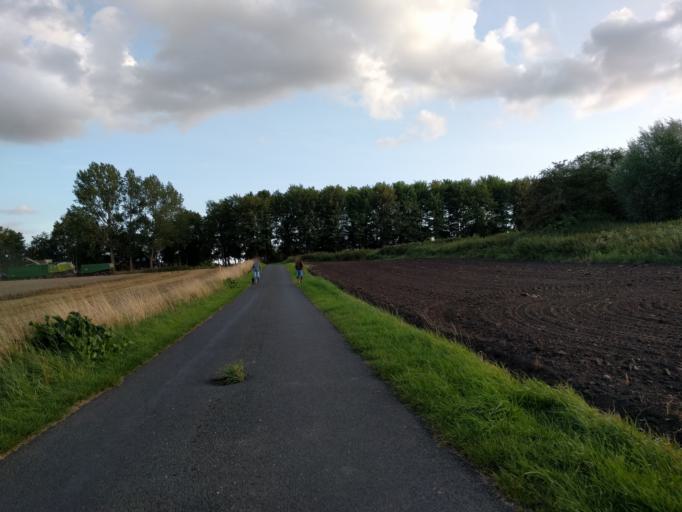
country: DK
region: South Denmark
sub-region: Kerteminde Kommune
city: Munkebo
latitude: 55.4688
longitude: 10.5801
